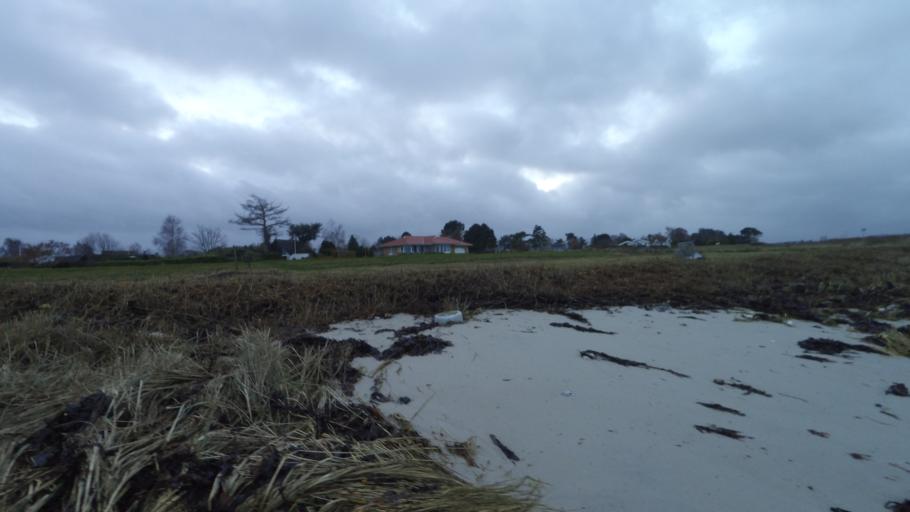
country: DK
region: Central Jutland
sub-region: Arhus Kommune
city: Beder
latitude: 56.0224
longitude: 10.2774
